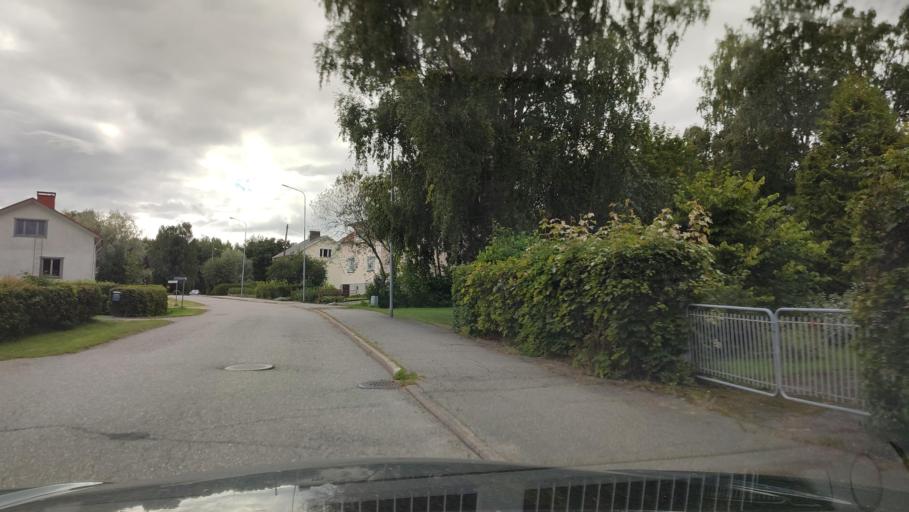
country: FI
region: Ostrobothnia
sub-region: Sydosterbotten
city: Kristinestad
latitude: 62.2718
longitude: 21.3722
